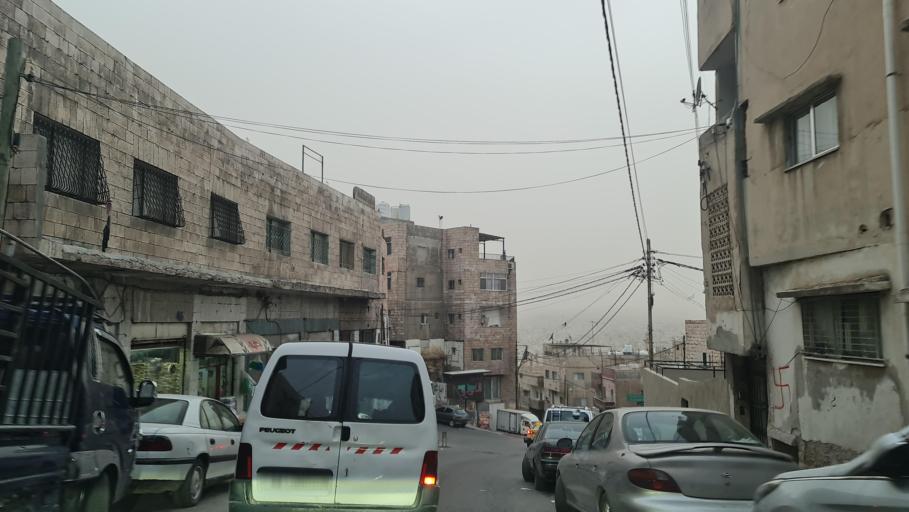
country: JO
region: Amman
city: Amman
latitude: 31.9460
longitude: 35.9441
